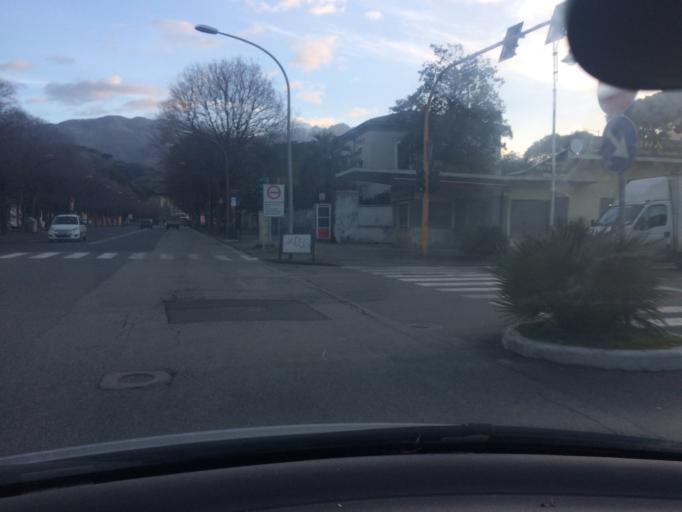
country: IT
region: Tuscany
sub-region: Provincia di Massa-Carrara
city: Carrara
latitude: 44.0652
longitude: 10.0745
